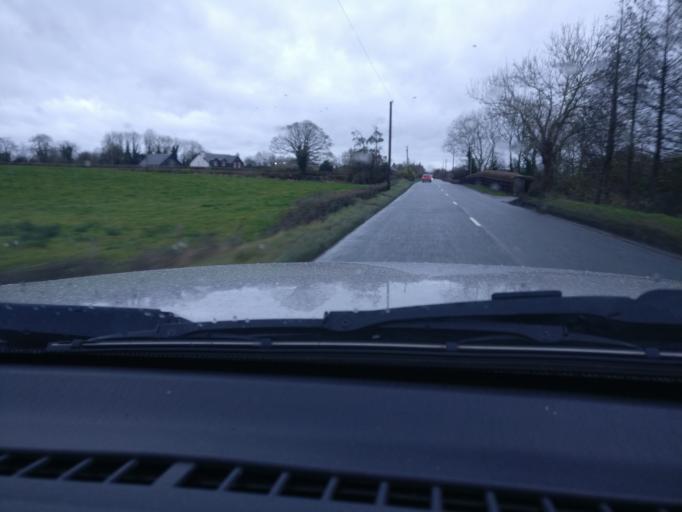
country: IE
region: Leinster
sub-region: An Mhi
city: Trim
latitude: 53.5342
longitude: -6.8114
